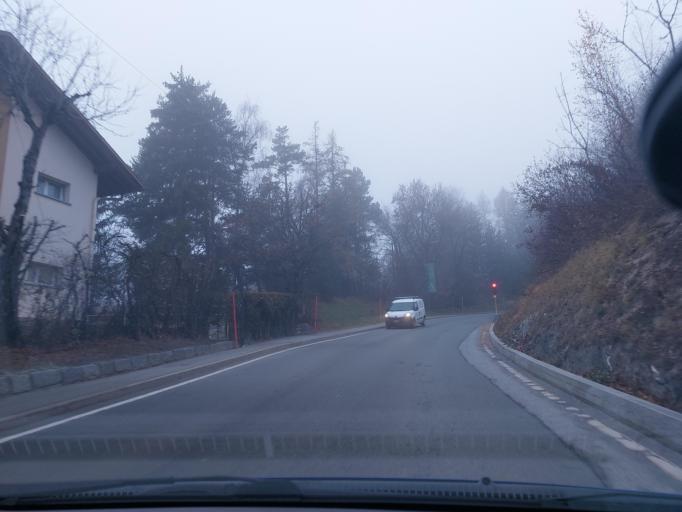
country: CH
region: Valais
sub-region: Sierre District
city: Lens
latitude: 46.2847
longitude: 7.4475
